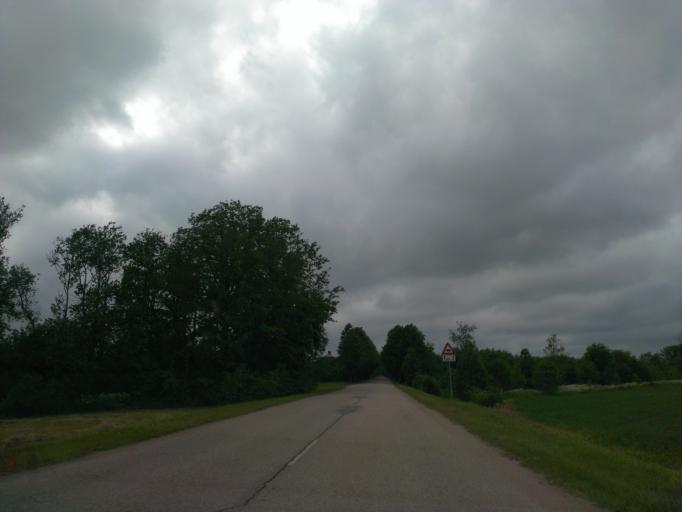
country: LV
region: Durbe
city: Liegi
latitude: 56.7295
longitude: 21.4042
